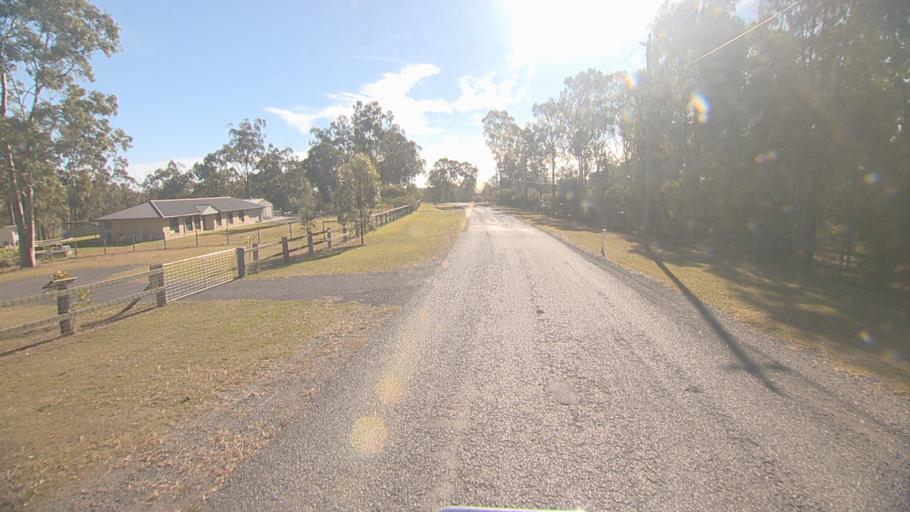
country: AU
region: Queensland
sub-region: Ipswich
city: Springfield Lakes
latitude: -27.7018
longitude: 152.9294
